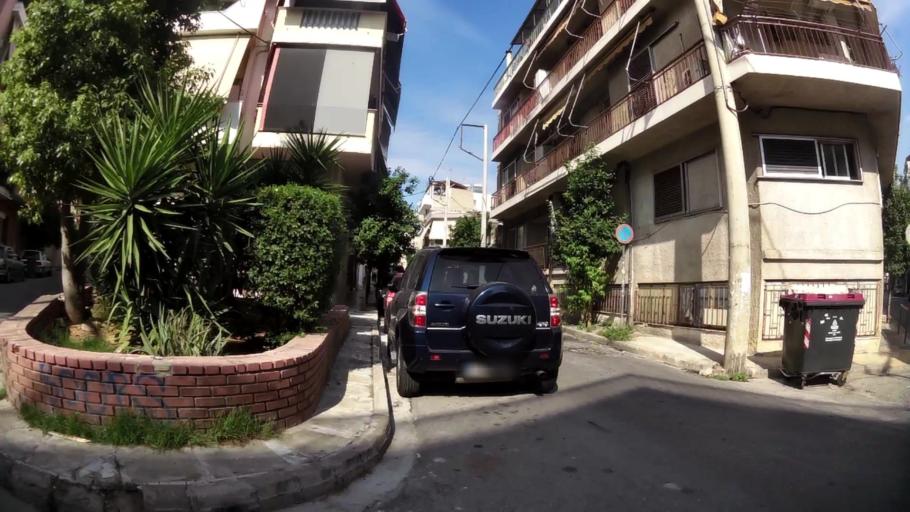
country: GR
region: Attica
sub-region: Nomos Piraios
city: Nikaia
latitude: 37.9625
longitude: 23.6475
